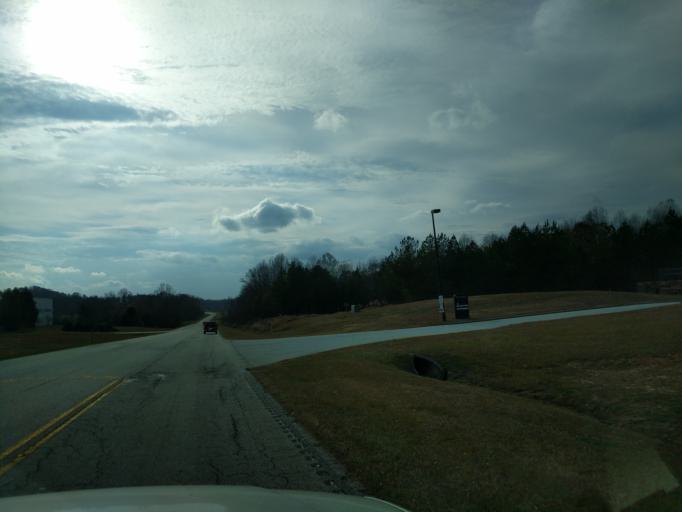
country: US
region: South Carolina
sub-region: Oconee County
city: Westminster
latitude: 34.6595
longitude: -83.0396
